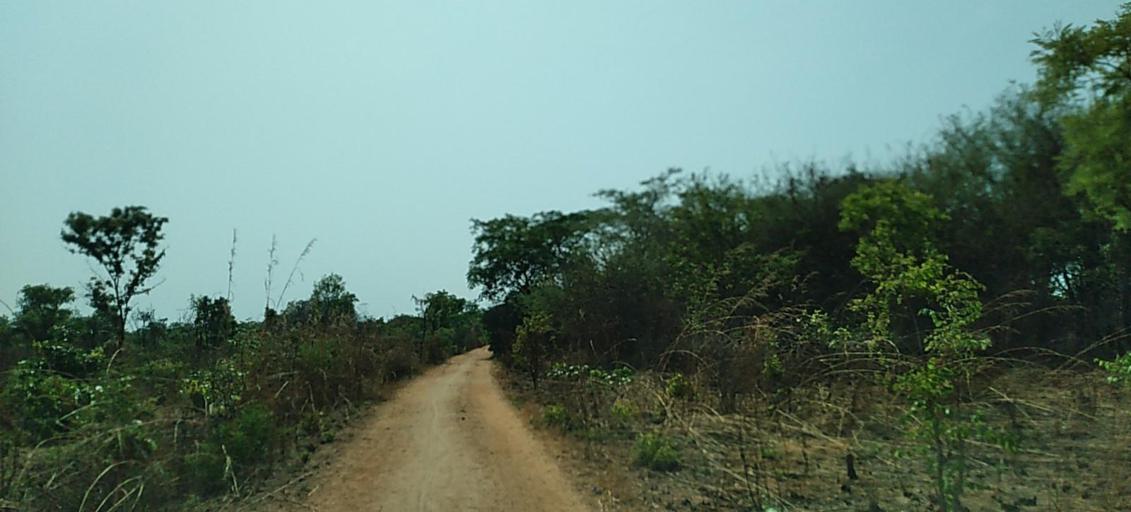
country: ZM
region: Copperbelt
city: Luanshya
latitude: -13.2817
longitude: 28.3202
